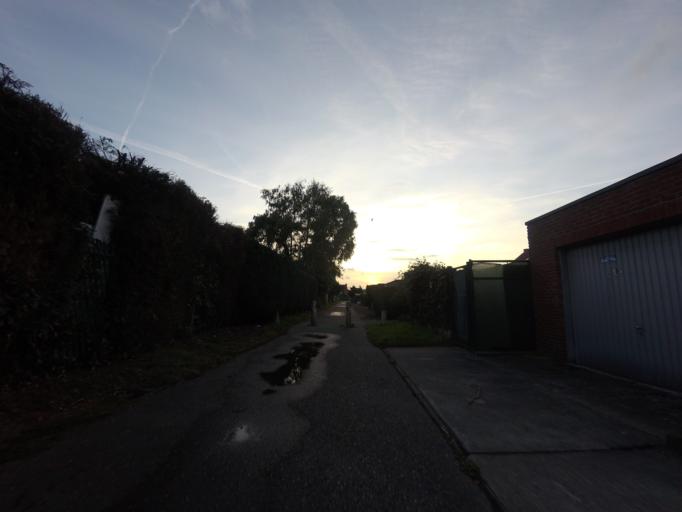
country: BE
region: Flanders
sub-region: Provincie Antwerpen
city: Willebroek
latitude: 51.0501
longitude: 4.3836
